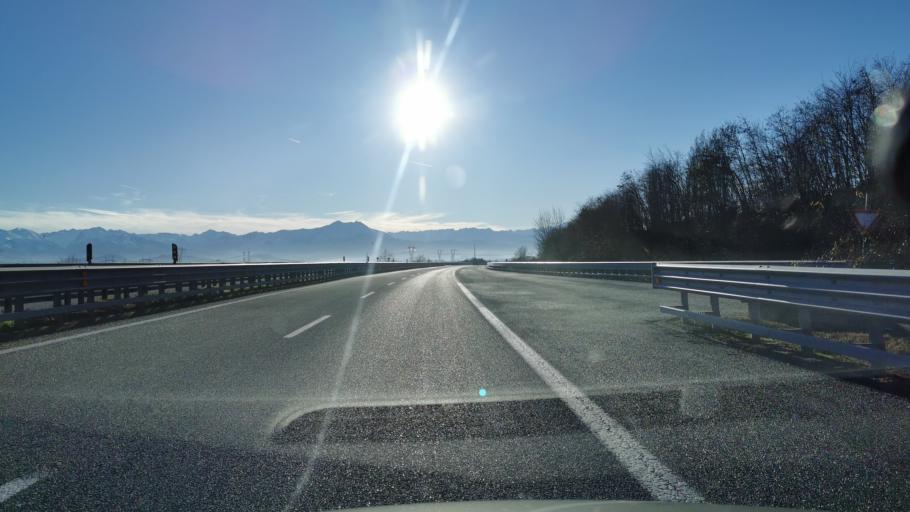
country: IT
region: Piedmont
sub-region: Provincia di Cuneo
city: Magliano Alpi
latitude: 44.4752
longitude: 7.7901
